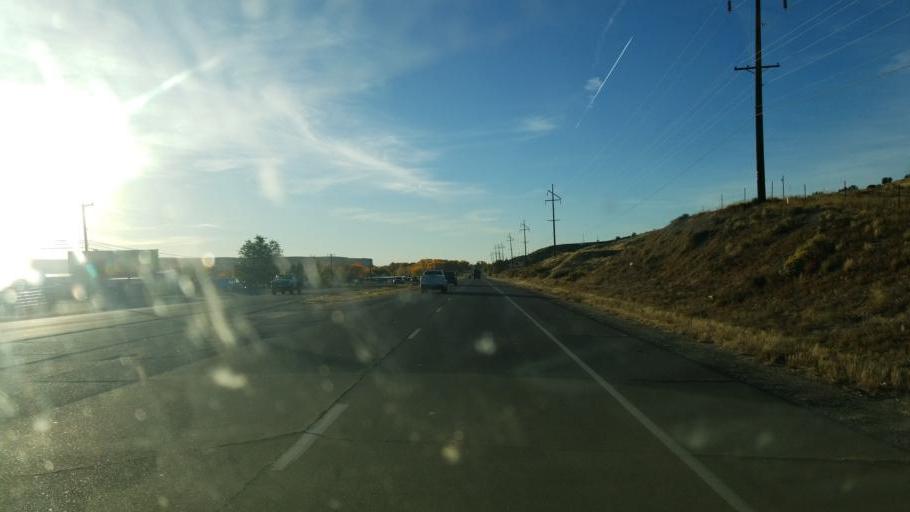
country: US
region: New Mexico
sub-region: San Juan County
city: Lee Acres
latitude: 36.7060
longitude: -108.1164
